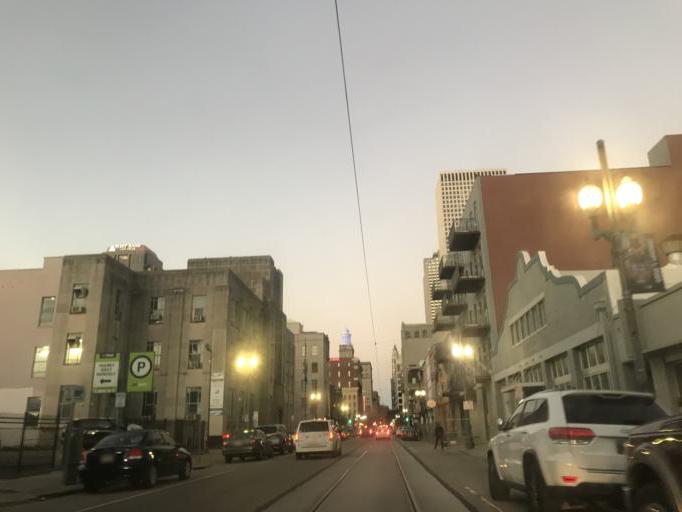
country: US
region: Louisiana
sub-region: Orleans Parish
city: New Orleans
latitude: 29.9465
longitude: -90.0728
